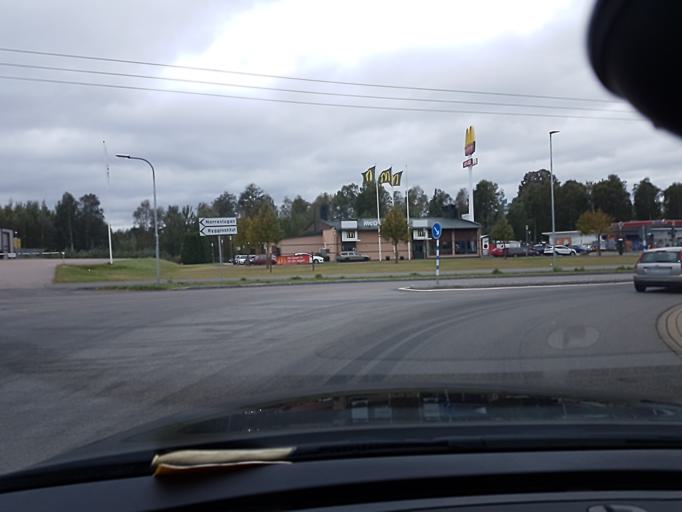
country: SE
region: Kronoberg
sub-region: Vaxjo Kommun
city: Vaexjoe
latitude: 56.9020
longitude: 14.8295
